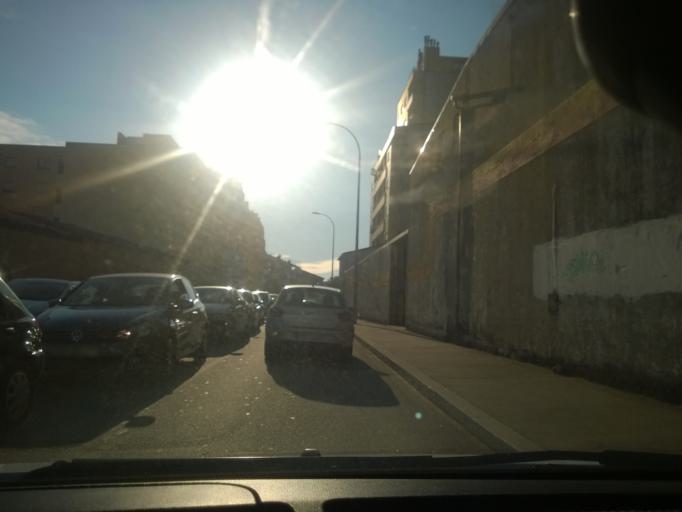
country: PT
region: Porto
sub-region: Porto
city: Porto
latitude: 41.1698
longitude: -8.6269
